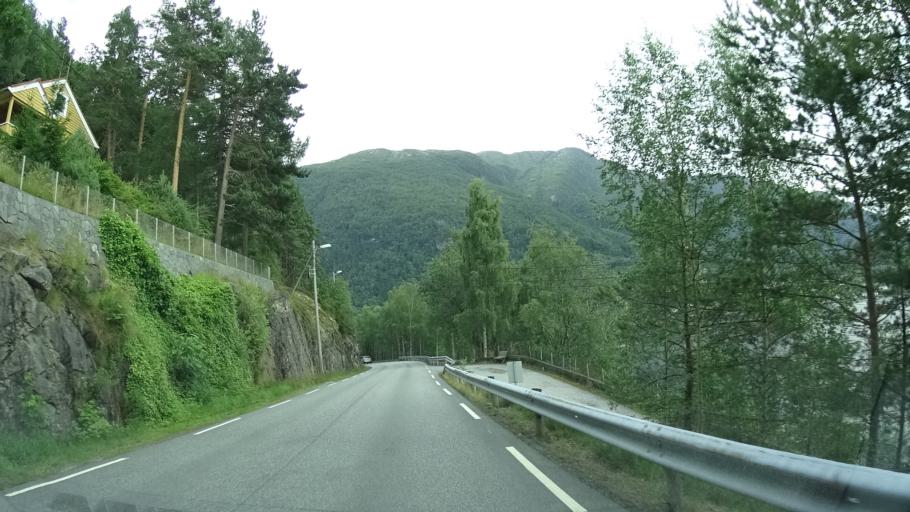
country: NO
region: Hordaland
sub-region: Jondal
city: Jondal
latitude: 60.2831
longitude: 6.2473
